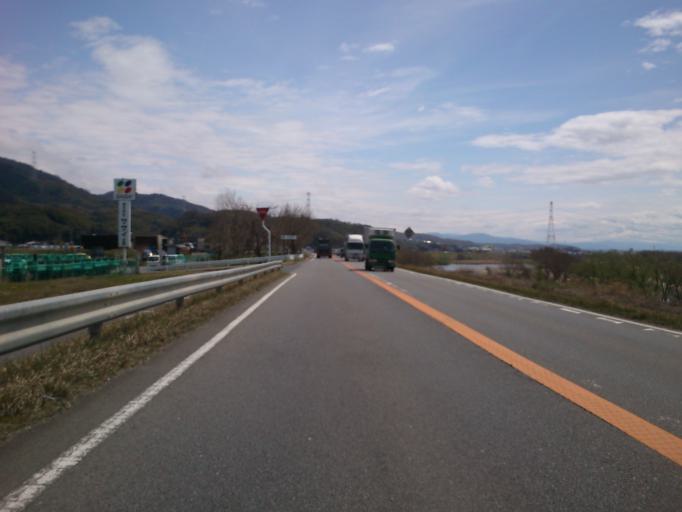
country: JP
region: Kyoto
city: Tanabe
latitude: 34.8160
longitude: 135.8009
